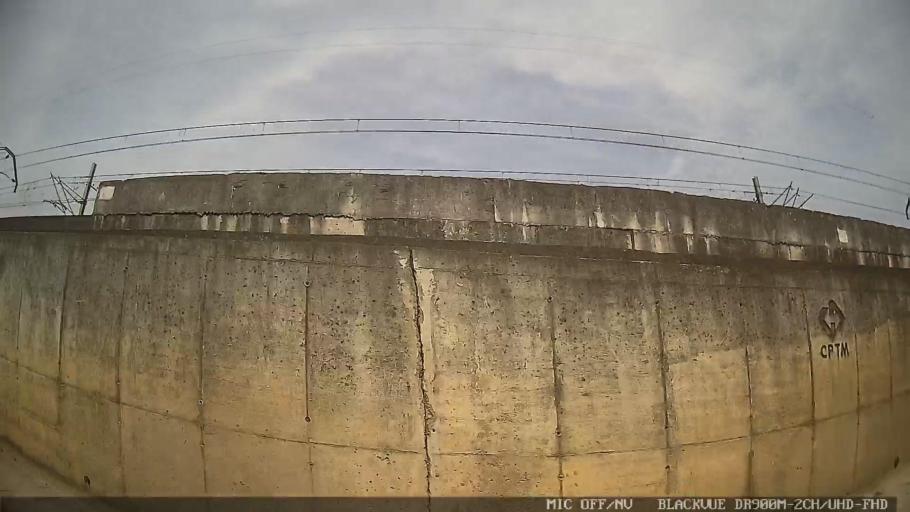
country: BR
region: Sao Paulo
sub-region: Itaquaquecetuba
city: Itaquaquecetuba
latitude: -23.4949
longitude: -46.3382
